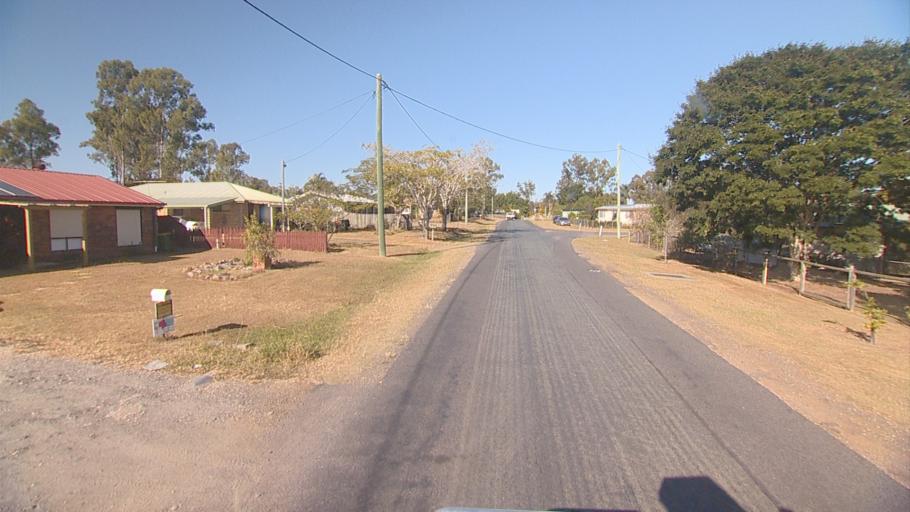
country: AU
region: Queensland
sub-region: Logan
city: Cedar Vale
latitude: -27.8325
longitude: 153.0318
